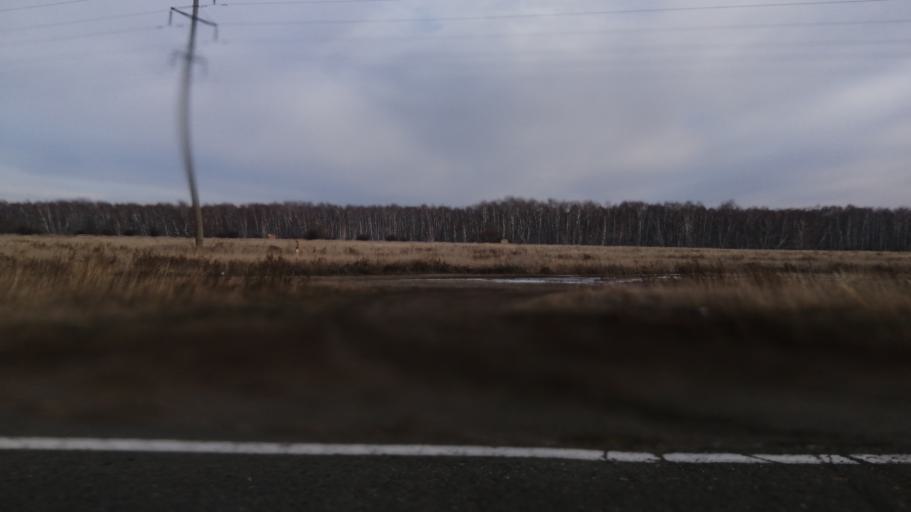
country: RU
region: Novosibirsk
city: Krasnozerskoye
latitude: 53.9882
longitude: 78.7327
